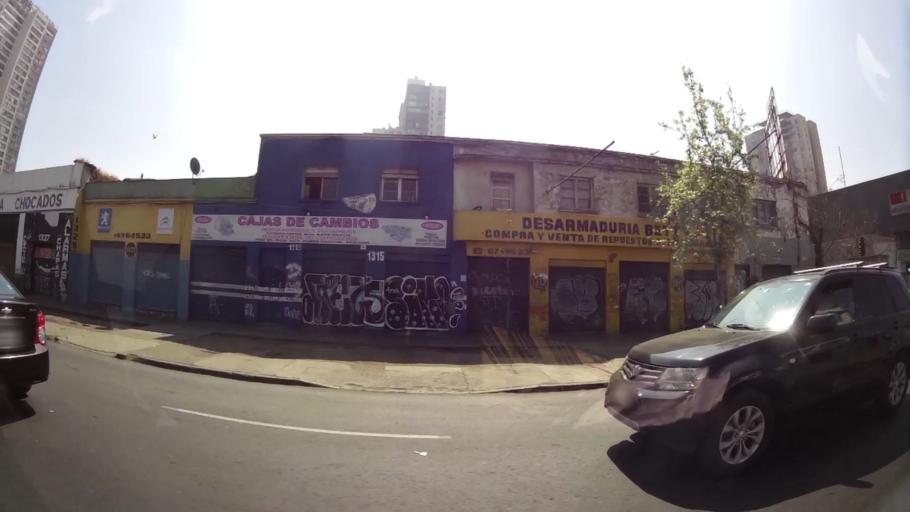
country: CL
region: Santiago Metropolitan
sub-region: Provincia de Santiago
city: Santiago
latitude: -33.4544
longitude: -70.6529
